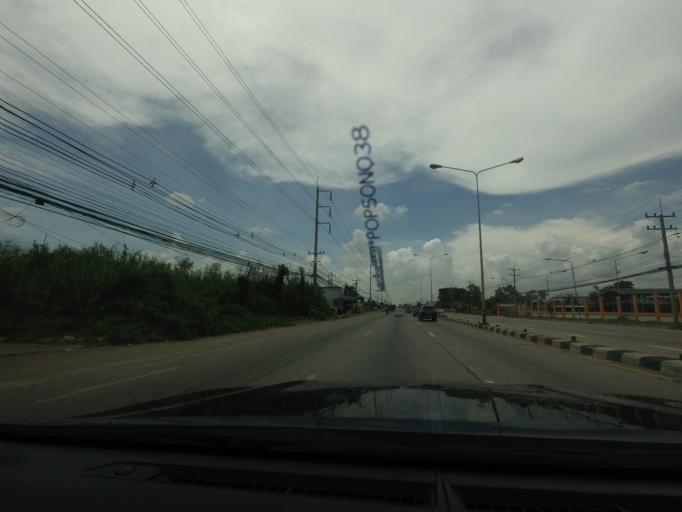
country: TH
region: Nakhon Pathom
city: Nakhon Pathom
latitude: 13.8596
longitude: 100.0116
